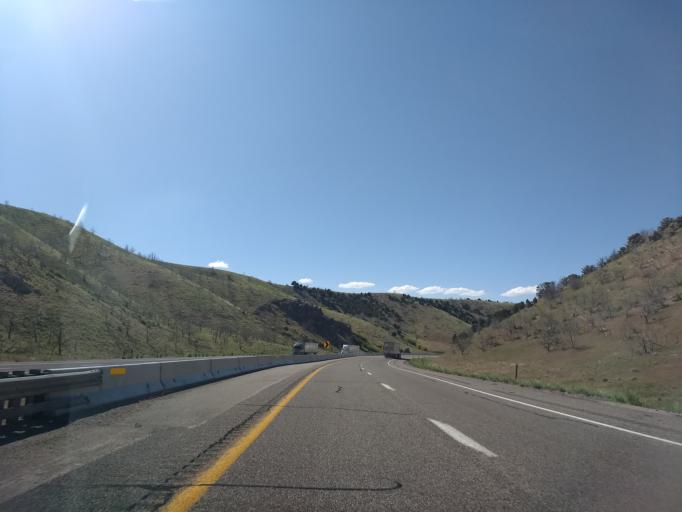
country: US
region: Utah
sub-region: Millard County
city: Fillmore
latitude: 38.6829
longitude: -112.5988
